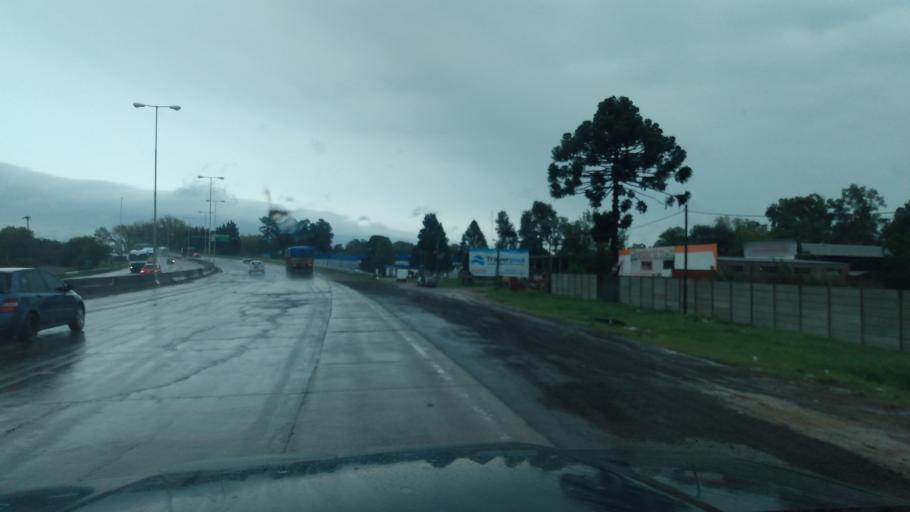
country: AR
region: Buenos Aires
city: Capilla del Senor
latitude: -34.3919
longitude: -59.0271
